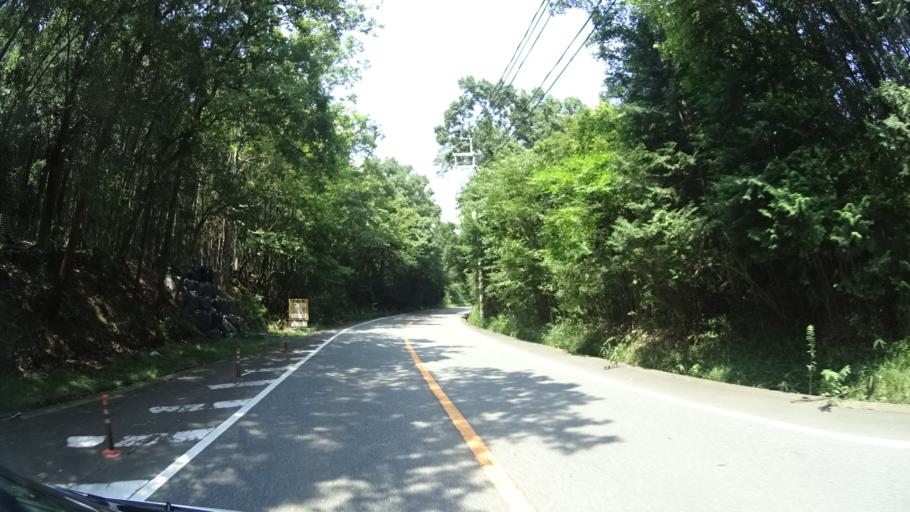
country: JP
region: Kyoto
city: Fukuchiyama
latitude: 35.2594
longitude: 135.1464
